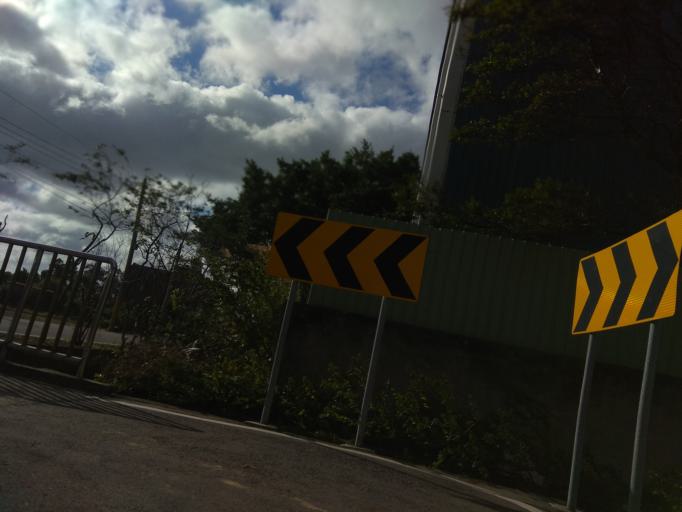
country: TW
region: Taiwan
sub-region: Hsinchu
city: Zhubei
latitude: 24.9741
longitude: 121.0872
